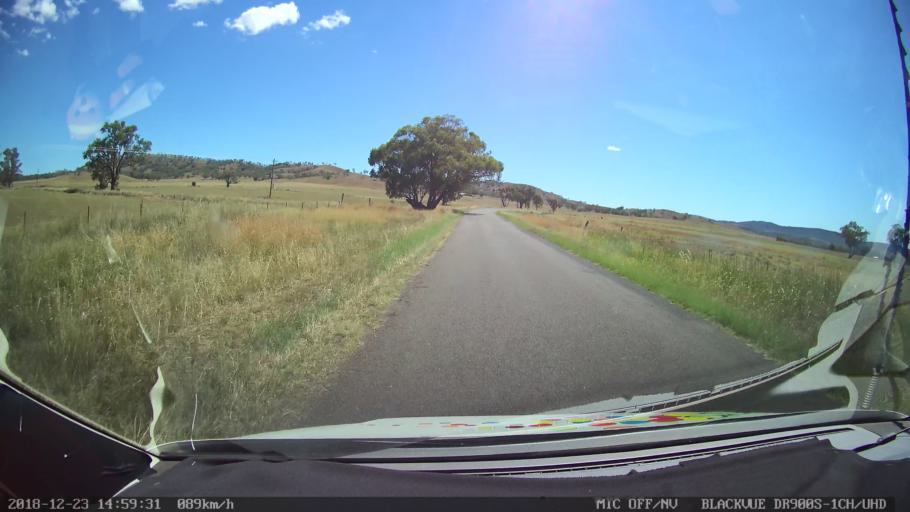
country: AU
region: New South Wales
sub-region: Tamworth Municipality
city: Manilla
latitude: -30.7244
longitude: 150.7996
